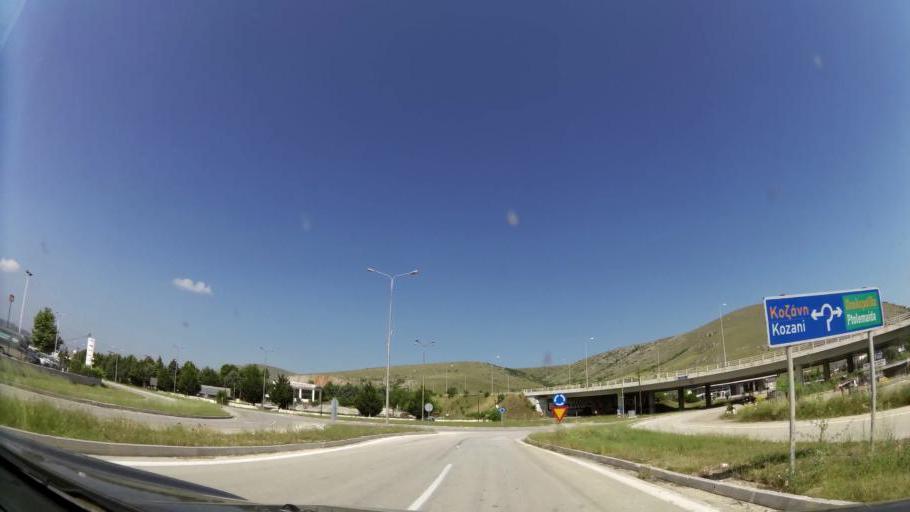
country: GR
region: West Macedonia
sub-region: Nomos Kozanis
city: Koila
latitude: 40.3455
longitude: 21.7997
